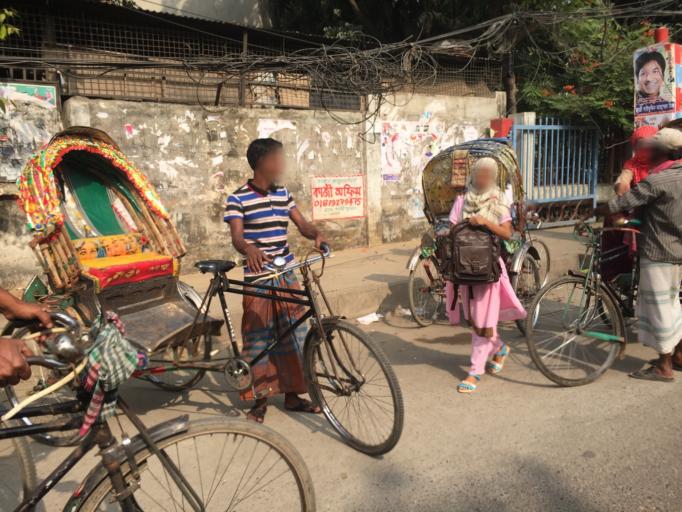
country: BD
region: Dhaka
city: Paltan
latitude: 23.7338
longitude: 90.4047
